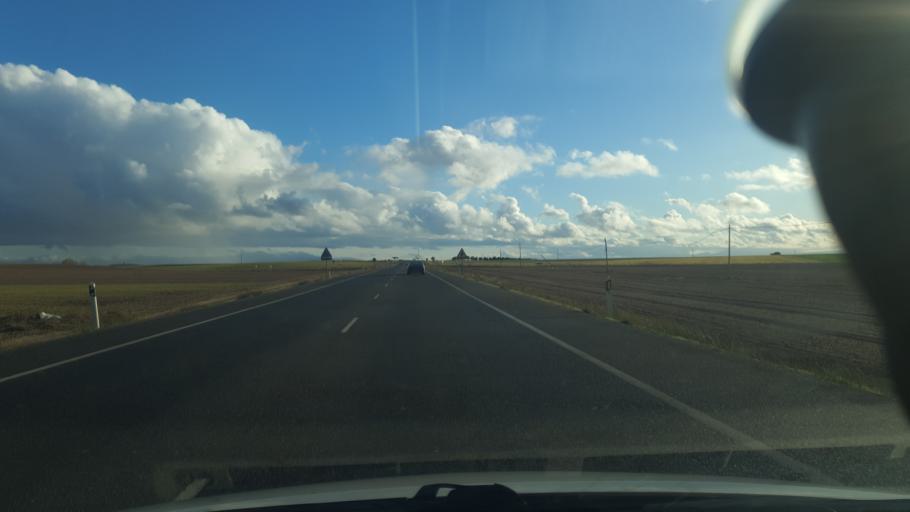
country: ES
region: Castille and Leon
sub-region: Provincia de Segovia
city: Rapariegos
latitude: 41.0931
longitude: -4.6381
